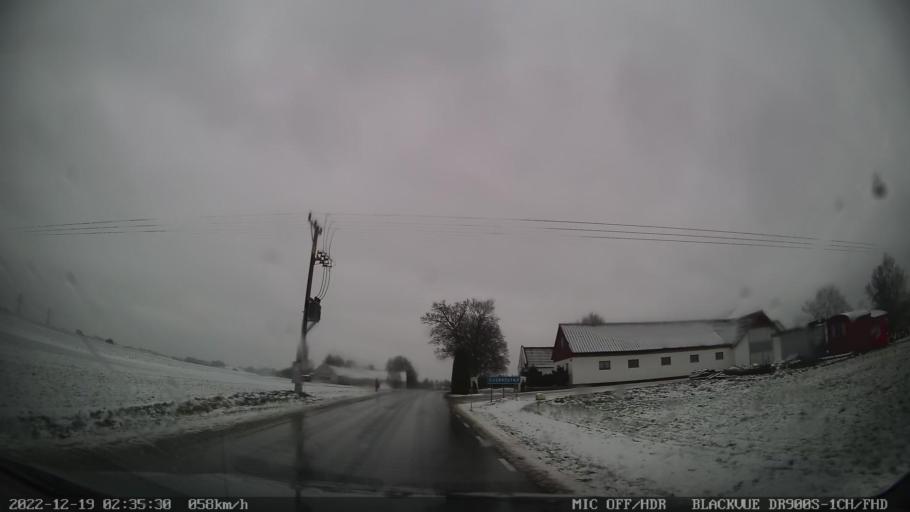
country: SE
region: Skane
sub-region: Tomelilla Kommun
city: Tomelilla
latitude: 55.5327
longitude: 14.0408
